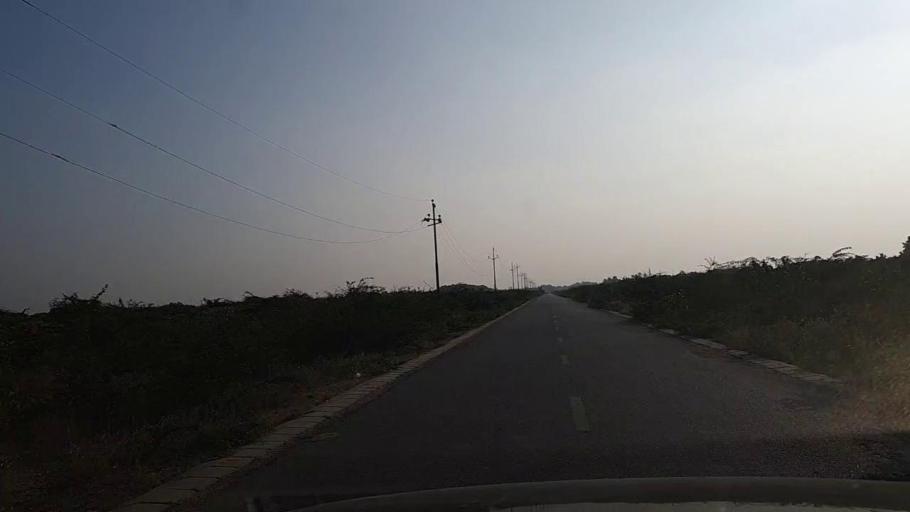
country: PK
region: Sindh
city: Gharo
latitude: 24.7913
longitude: 67.5162
